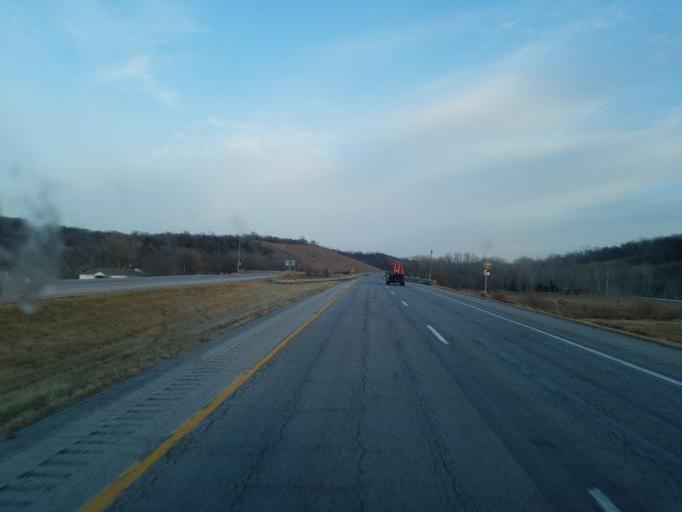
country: US
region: Iowa
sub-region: Harrison County
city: Missouri Valley
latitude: 41.4948
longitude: -95.8935
